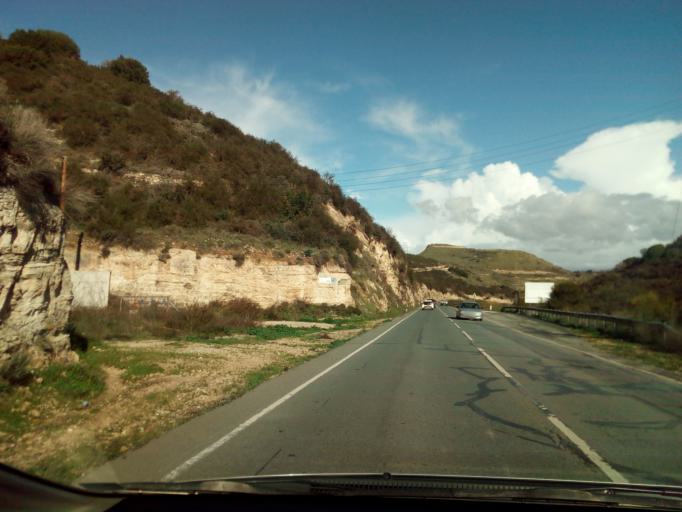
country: CY
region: Pafos
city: Mesogi
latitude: 34.8619
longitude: 32.4814
